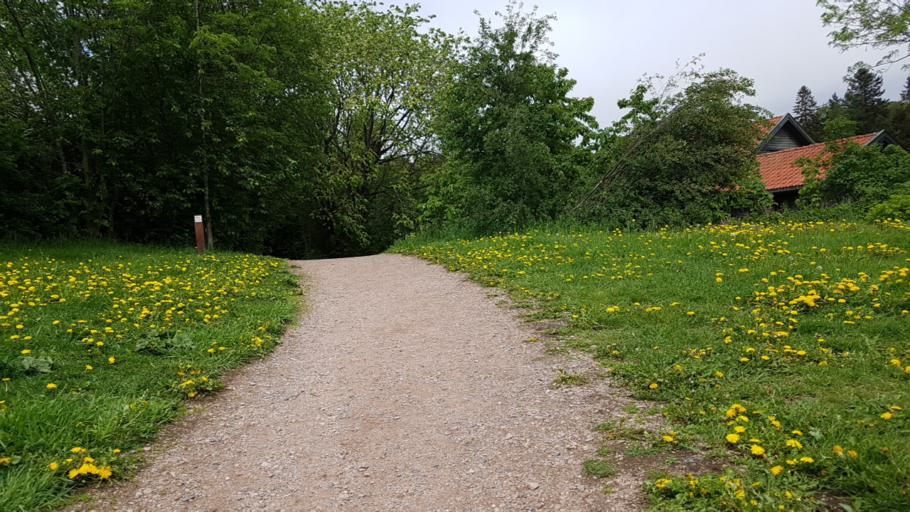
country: NO
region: Oslo
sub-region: Oslo
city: Oslo
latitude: 59.9418
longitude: 10.8220
